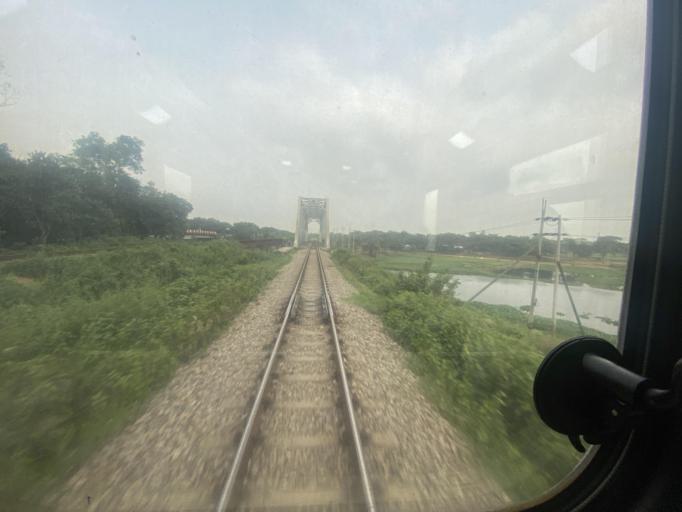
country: BD
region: Dhaka
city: Tungi
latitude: 23.9349
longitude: 90.4908
